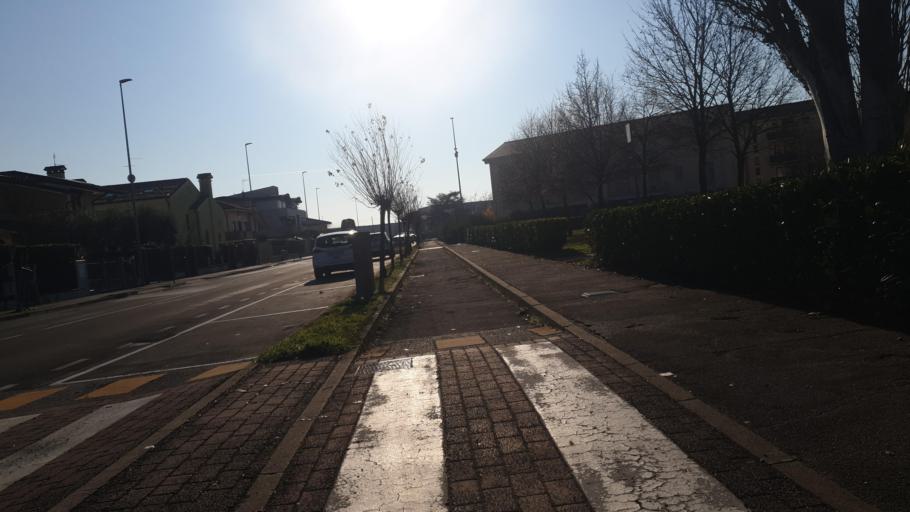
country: IT
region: Veneto
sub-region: Provincia di Padova
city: Masera di Padova
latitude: 45.3173
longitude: 11.8662
